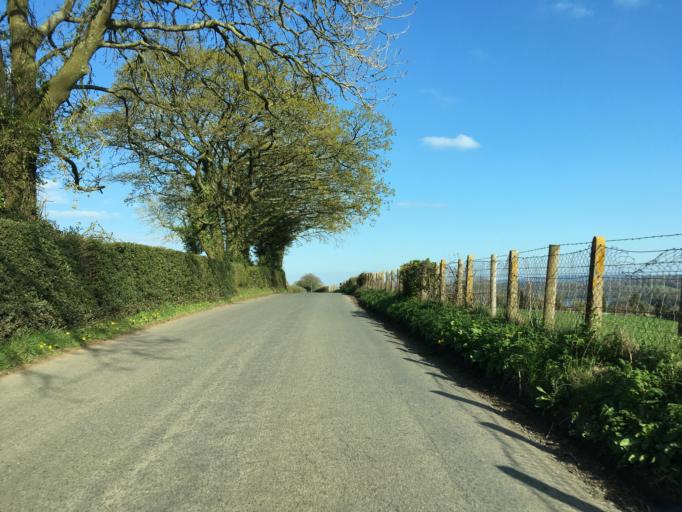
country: GB
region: Wales
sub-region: Torfaen County Borough
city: New Inn
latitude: 51.6993
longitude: -2.9945
